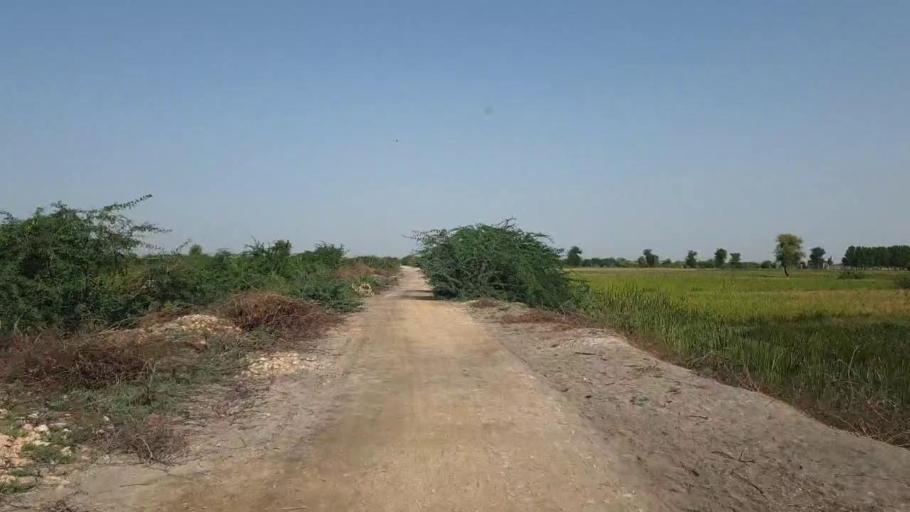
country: PK
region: Sindh
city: Tando Bago
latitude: 24.7176
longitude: 69.0728
